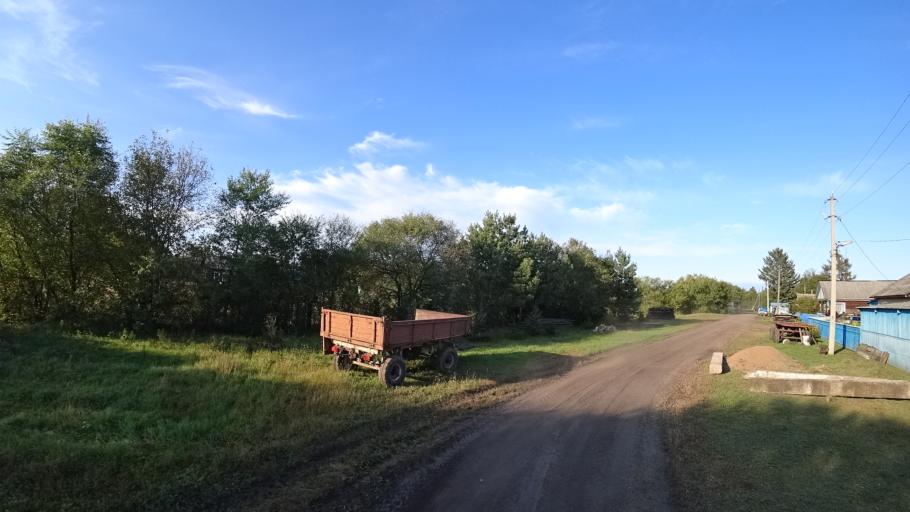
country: RU
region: Amur
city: Arkhara
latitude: 49.3604
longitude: 130.1271
